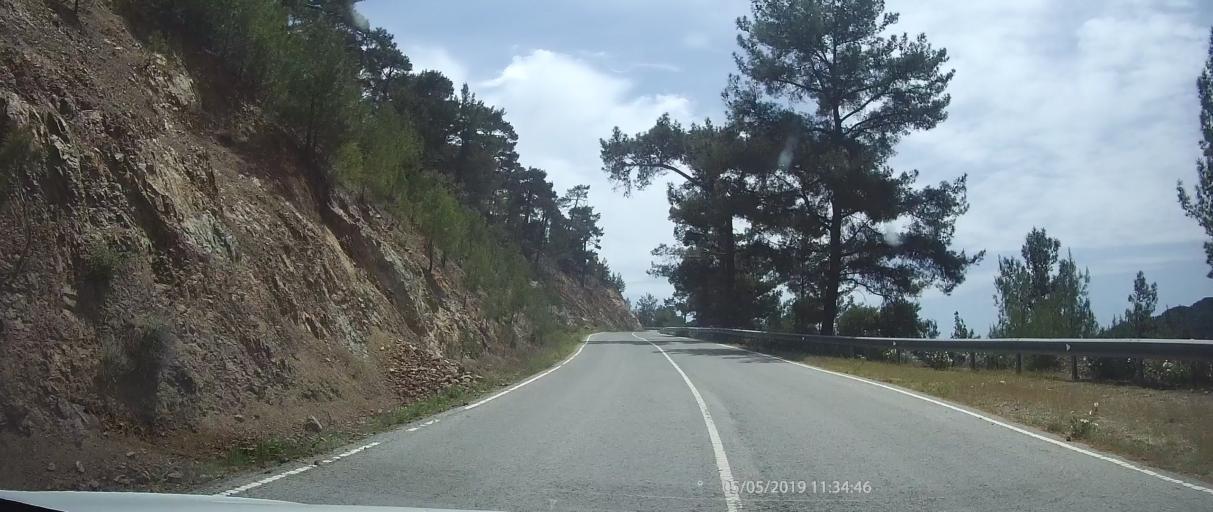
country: CY
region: Lefkosia
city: Kato Pyrgos
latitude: 34.9669
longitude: 32.6493
